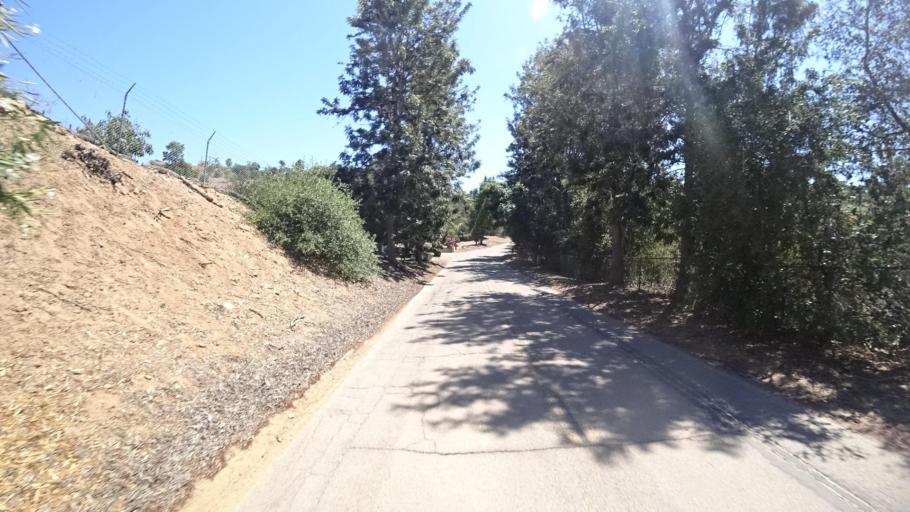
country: US
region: California
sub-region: San Diego County
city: Rainbow
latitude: 33.3537
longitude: -117.1780
